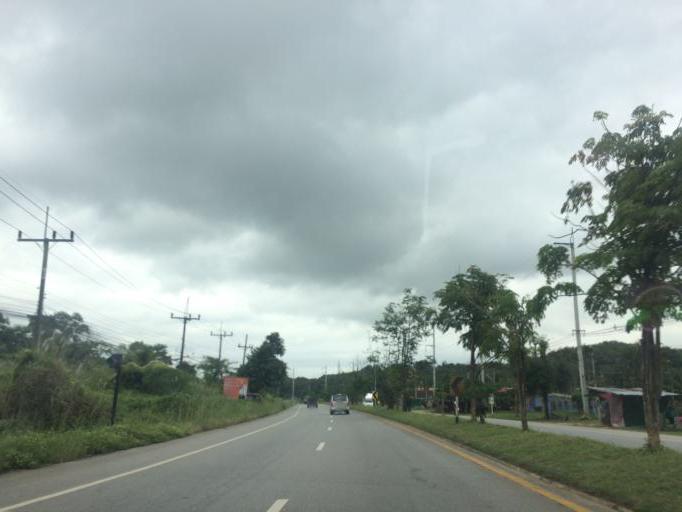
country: TH
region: Chiang Rai
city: Mae Chan
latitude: 20.1241
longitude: 99.8679
